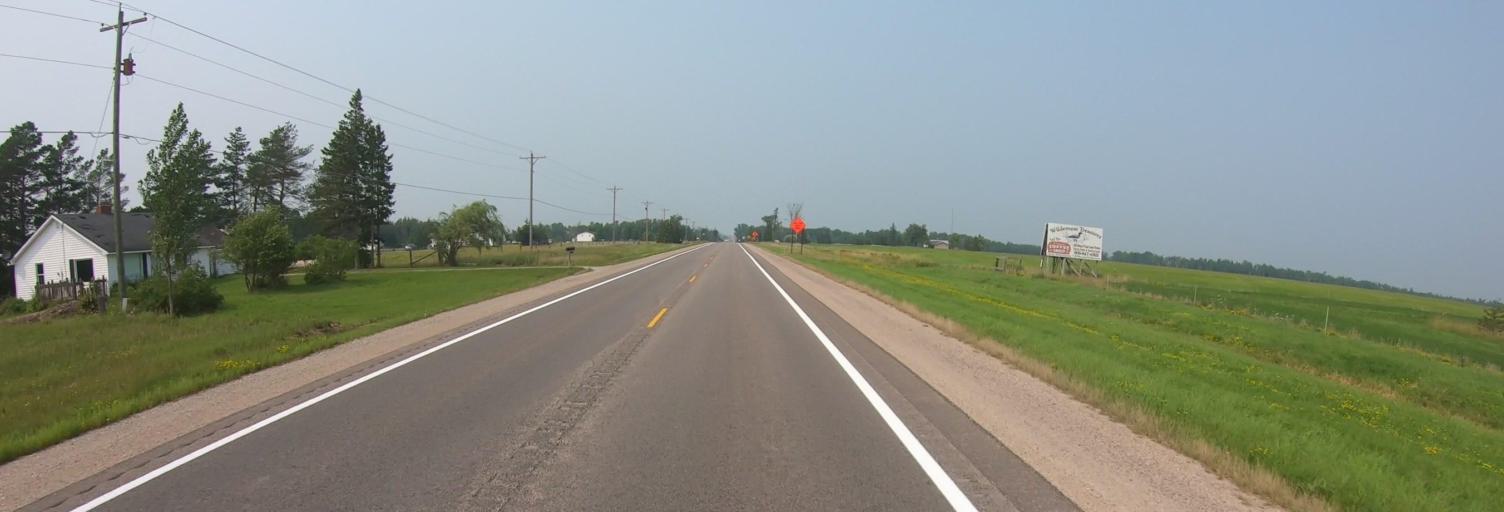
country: US
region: Michigan
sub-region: Chippewa County
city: Sault Ste. Marie
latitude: 46.1362
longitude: -84.3633
